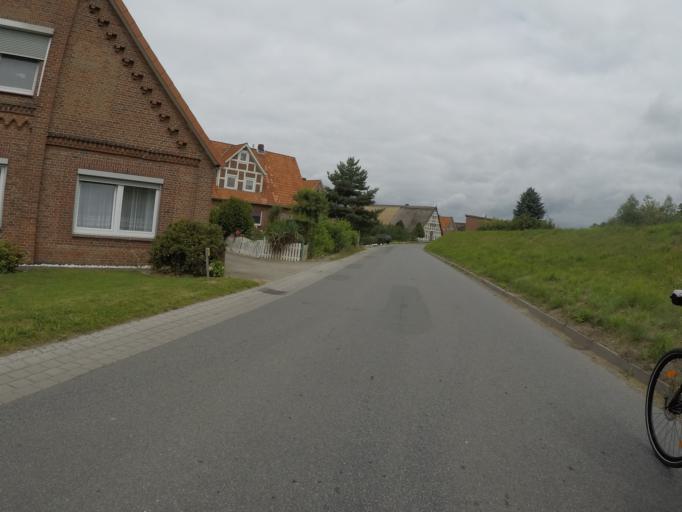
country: DE
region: Lower Saxony
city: Guderhandviertel
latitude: 53.5446
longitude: 9.6111
